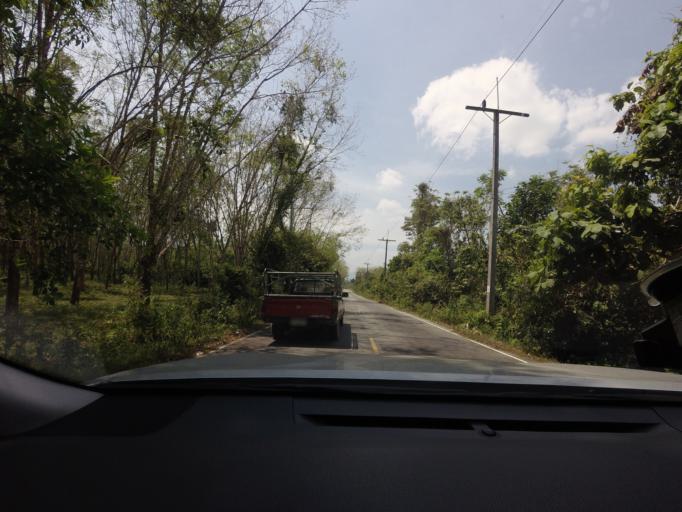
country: TH
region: Narathiwat
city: Rueso
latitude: 6.3843
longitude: 101.5072
